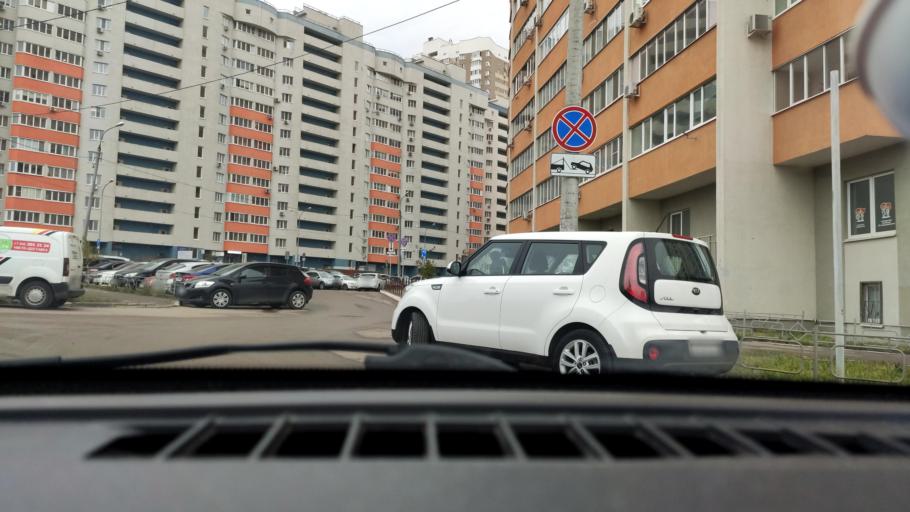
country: RU
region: Samara
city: Samara
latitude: 53.2189
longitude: 50.1714
